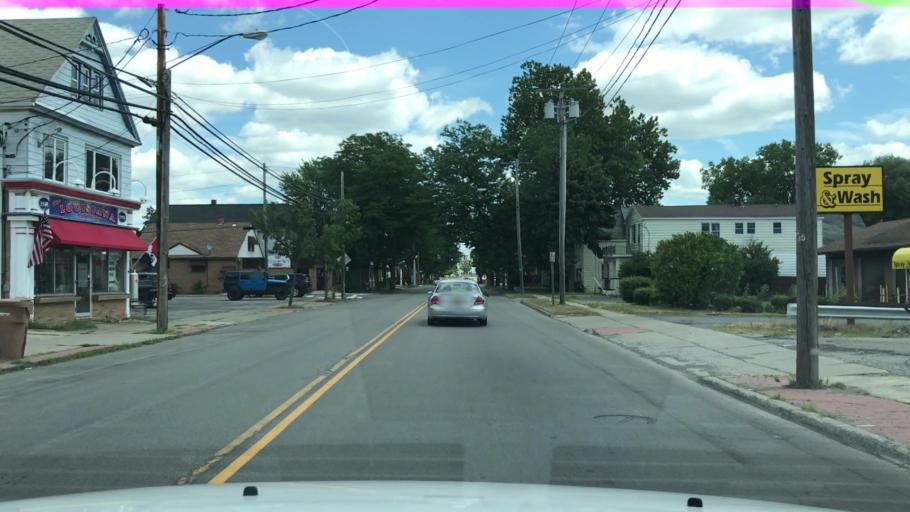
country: US
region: New York
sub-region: Erie County
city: Sloan
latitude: 42.9073
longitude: -78.7904
